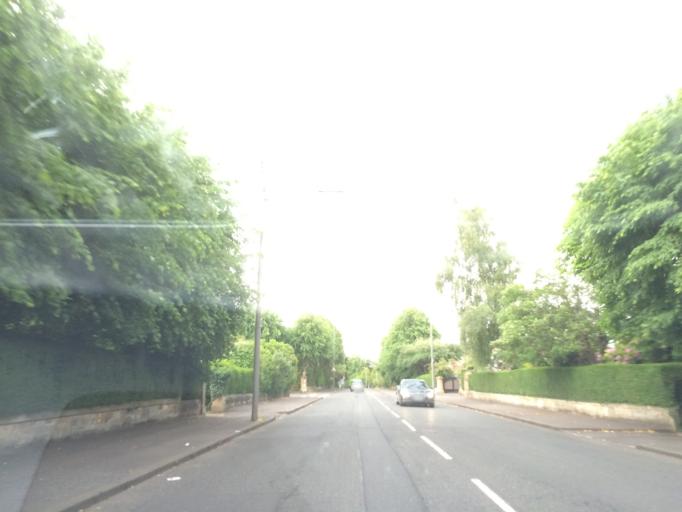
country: GB
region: Scotland
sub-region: East Renfrewshire
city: Giffnock
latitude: 55.8164
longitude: -4.2781
